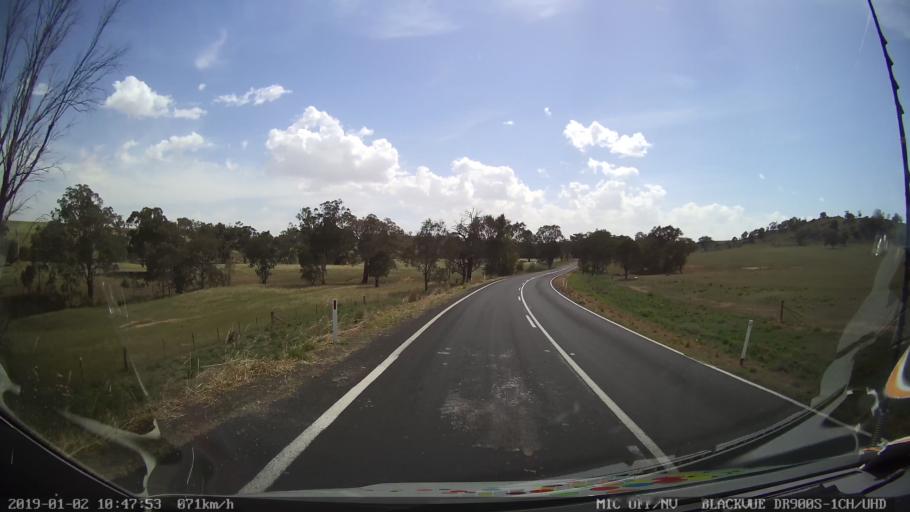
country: AU
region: New South Wales
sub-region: Cootamundra
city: Cootamundra
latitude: -34.7406
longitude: 148.2729
